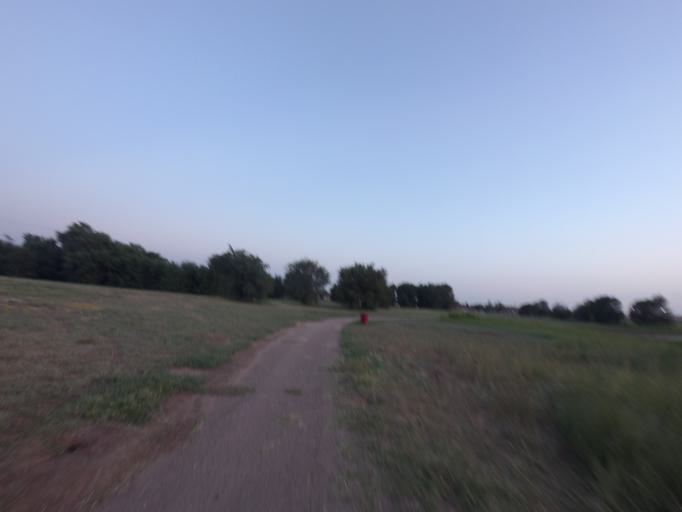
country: US
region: New Mexico
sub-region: Curry County
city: Clovis
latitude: 34.4288
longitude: -103.1885
